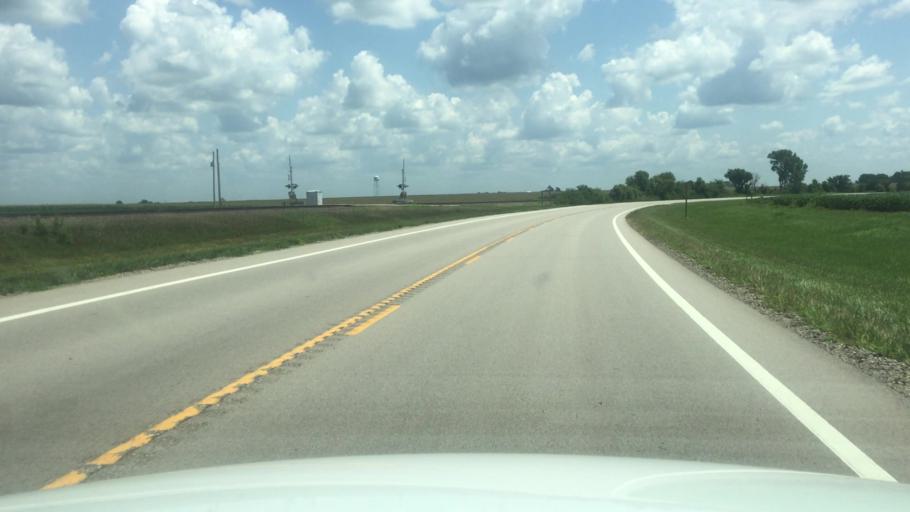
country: US
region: Kansas
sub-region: Brown County
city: Horton
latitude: 39.6513
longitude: -95.3599
